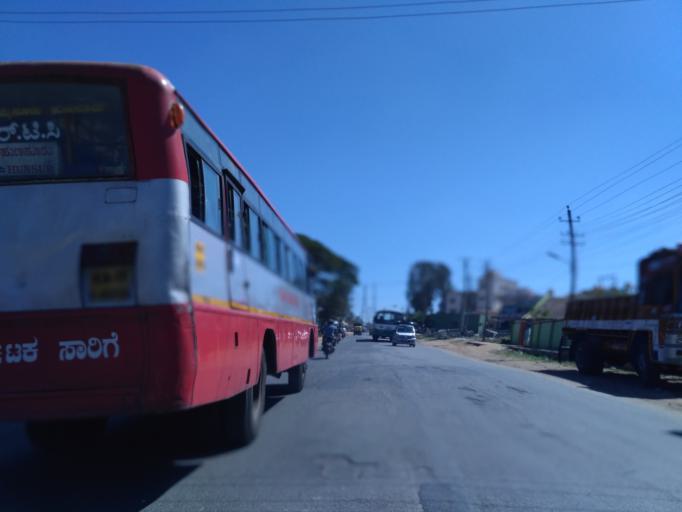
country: IN
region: Karnataka
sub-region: Hassan
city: Hassan
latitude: 12.9909
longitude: 76.1052
